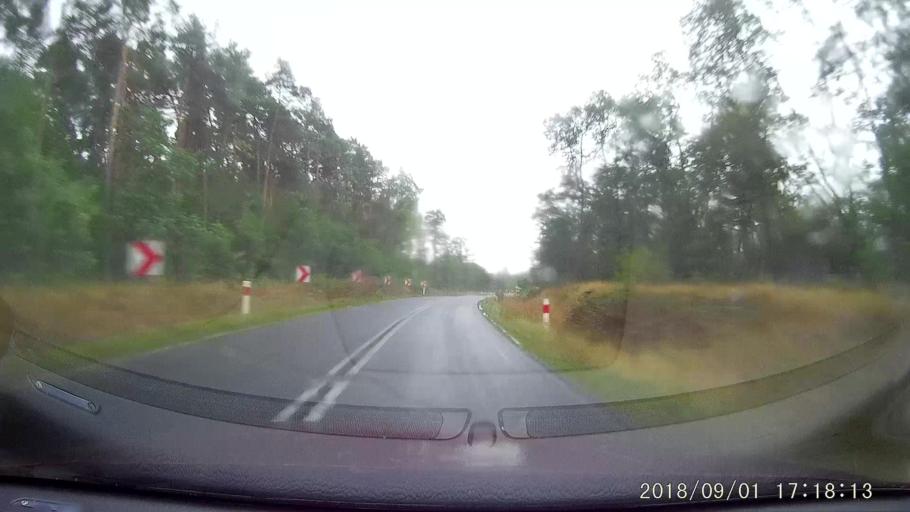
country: PL
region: Lubusz
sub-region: Powiat zielonogorski
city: Nowogrod Bobrzanski
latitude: 51.7403
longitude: 15.2712
